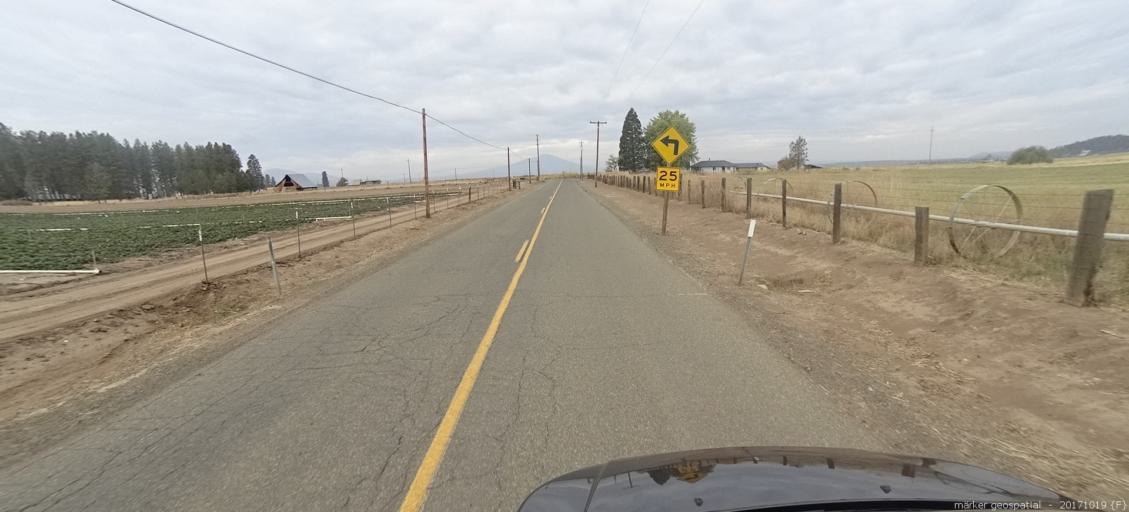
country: US
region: California
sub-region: Shasta County
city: Burney
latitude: 41.0805
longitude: -121.3484
